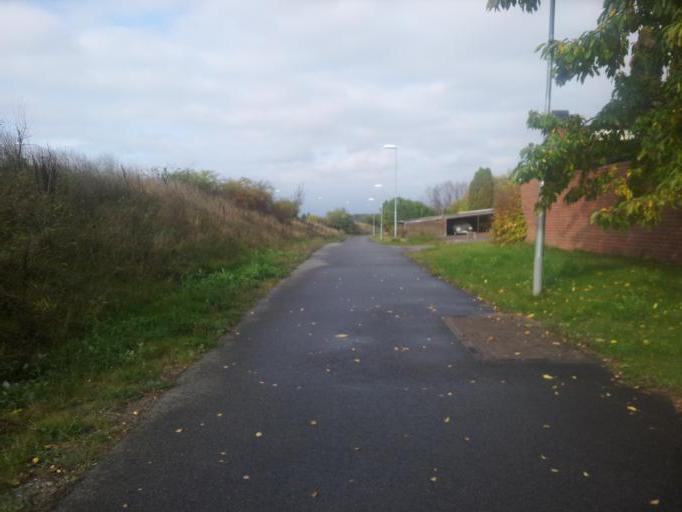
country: SE
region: Uppsala
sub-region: Uppsala Kommun
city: Uppsala
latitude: 59.8793
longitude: 17.6759
